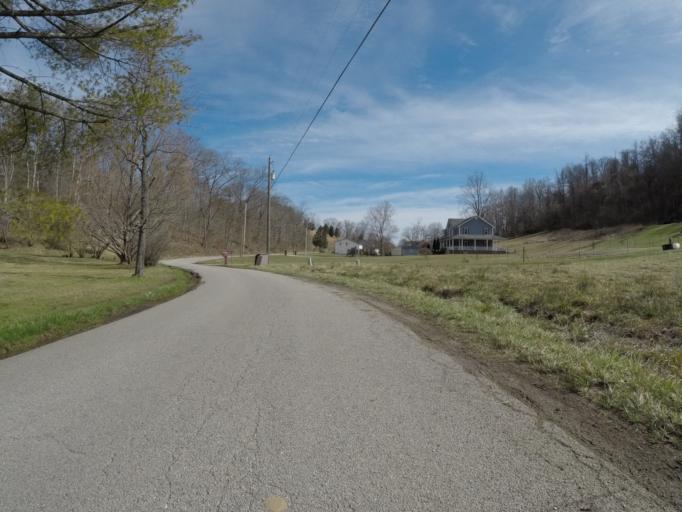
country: US
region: Ohio
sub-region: Lawrence County
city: Burlington
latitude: 38.3485
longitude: -82.5095
